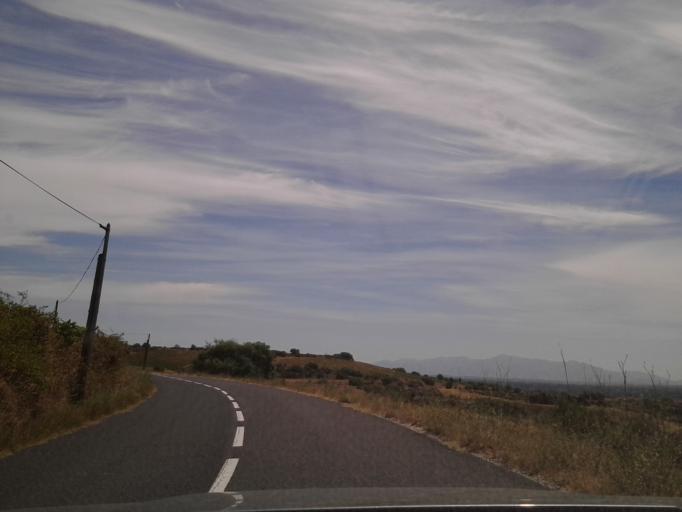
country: FR
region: Languedoc-Roussillon
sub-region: Departement des Pyrenees-Orientales
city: Millas
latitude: 42.7143
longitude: 2.6782
